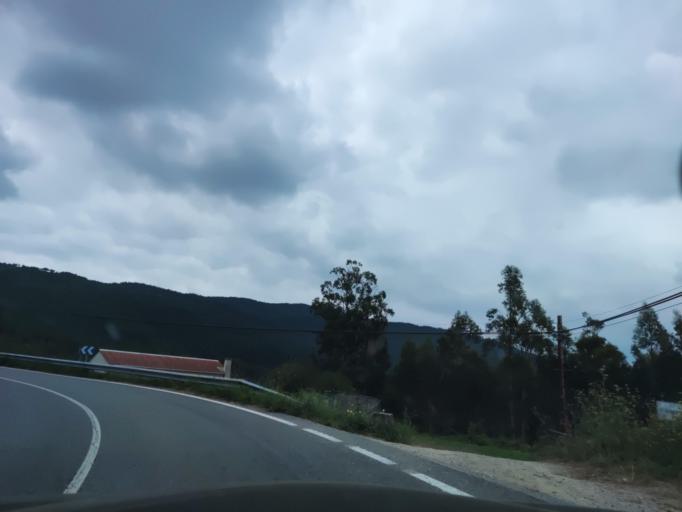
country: ES
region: Galicia
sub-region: Provincia da Coruna
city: Padron
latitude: 42.7374
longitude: -8.6275
